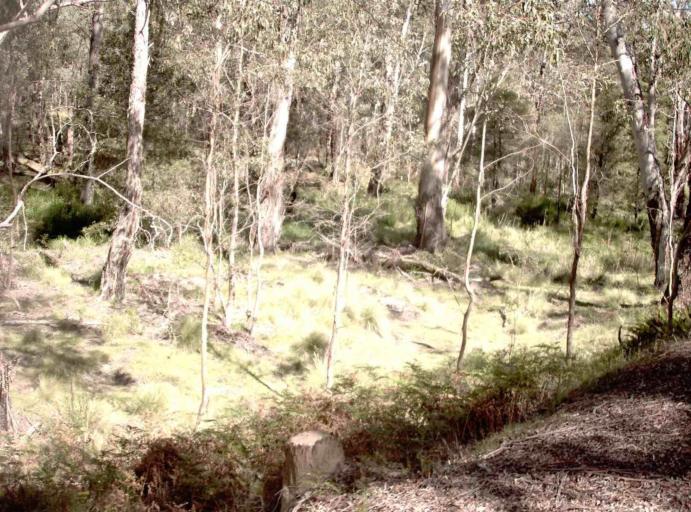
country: AU
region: New South Wales
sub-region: Bombala
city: Bombala
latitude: -37.1512
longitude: 148.7240
